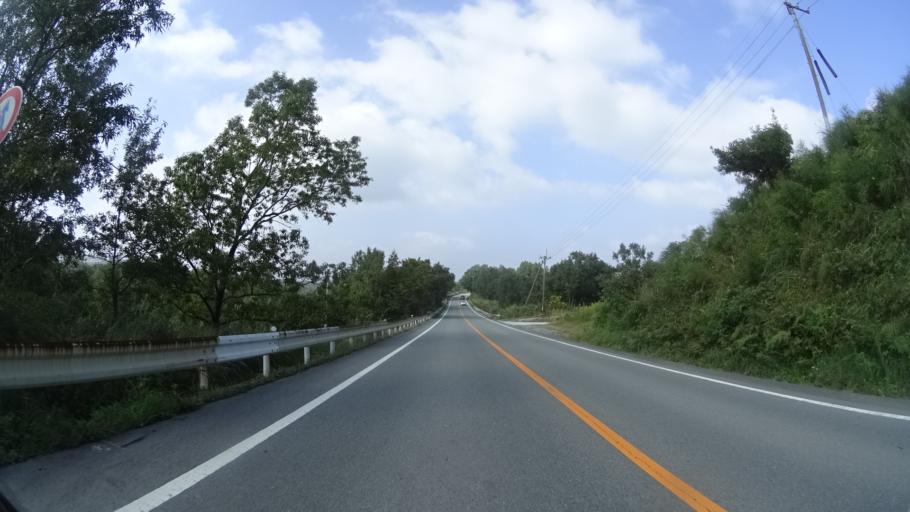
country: JP
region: Kumamoto
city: Aso
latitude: 33.0445
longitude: 131.0683
